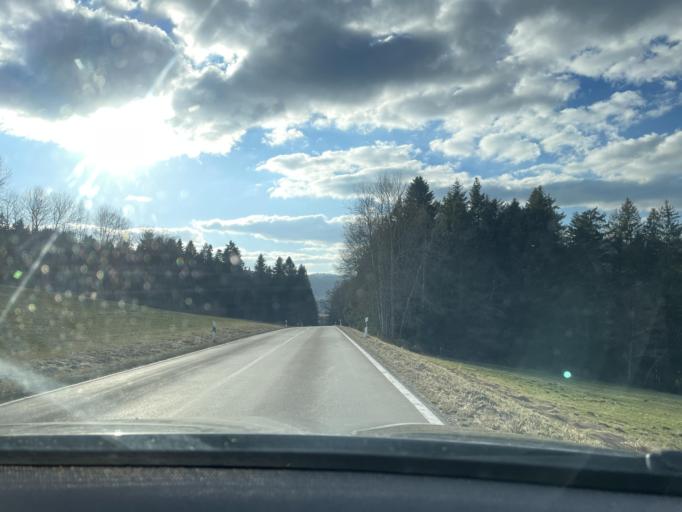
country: DE
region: Bavaria
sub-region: Lower Bavaria
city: Kollnburg
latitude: 49.0653
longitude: 12.8689
